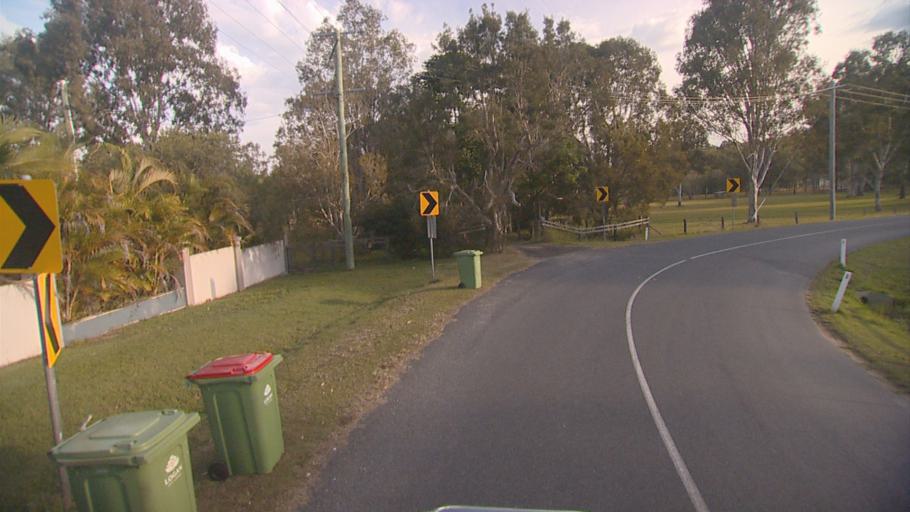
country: AU
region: Queensland
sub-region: Logan
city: Cedar Vale
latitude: -27.8396
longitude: 153.1052
